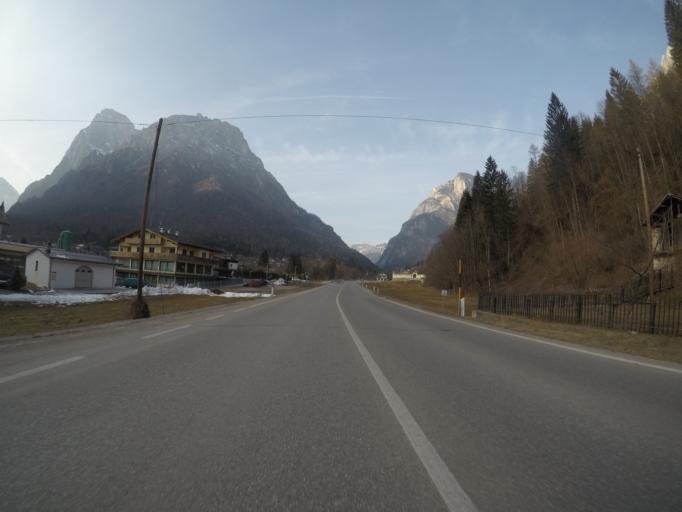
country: IT
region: Veneto
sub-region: Provincia di Belluno
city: Taibon Agordino
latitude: 46.3008
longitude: 12.0148
